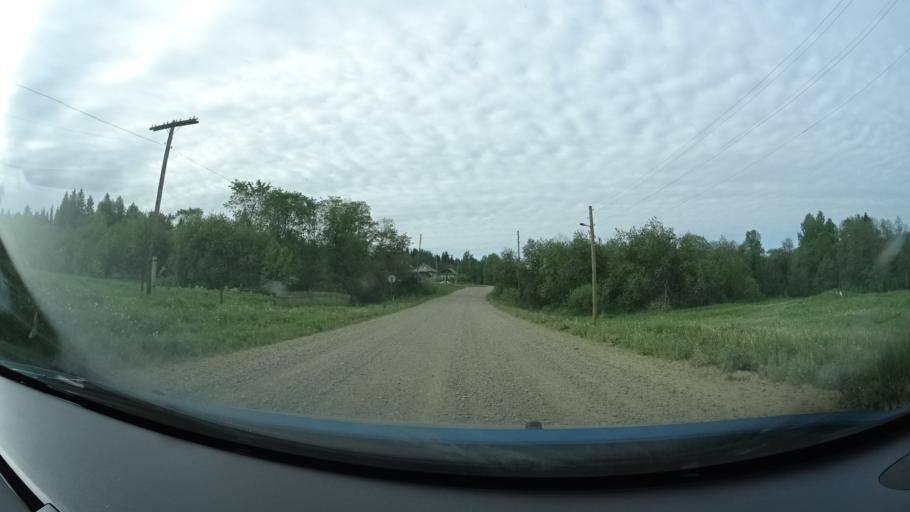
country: RU
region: Perm
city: Kuyeda
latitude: 56.6613
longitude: 55.6931
